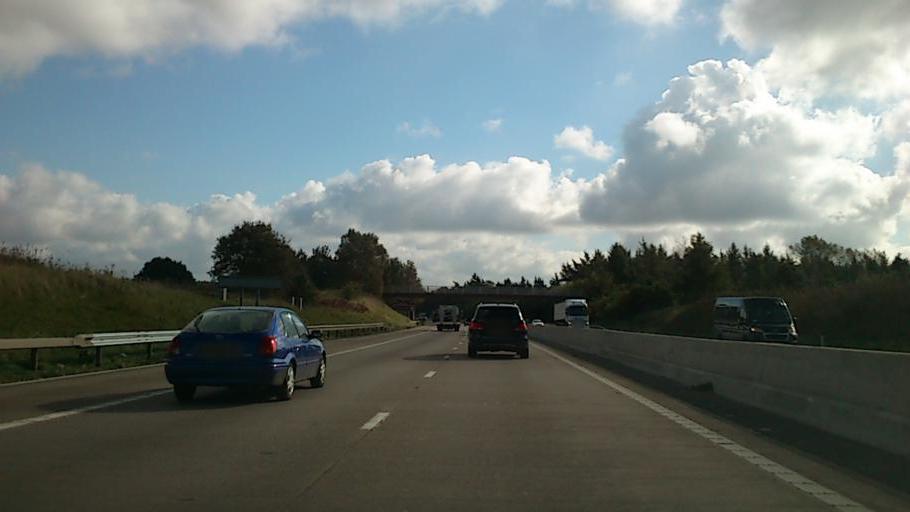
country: GB
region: England
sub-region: Shropshire
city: Tong
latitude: 52.6648
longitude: -2.3240
